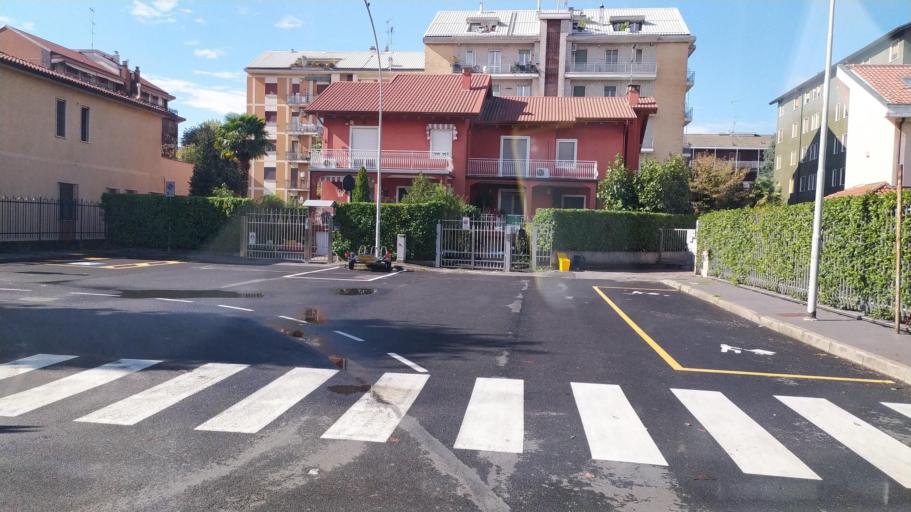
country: IT
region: Lombardy
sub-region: Citta metropolitana di Milano
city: Trezzano sul Naviglio
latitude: 45.4248
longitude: 9.0607
